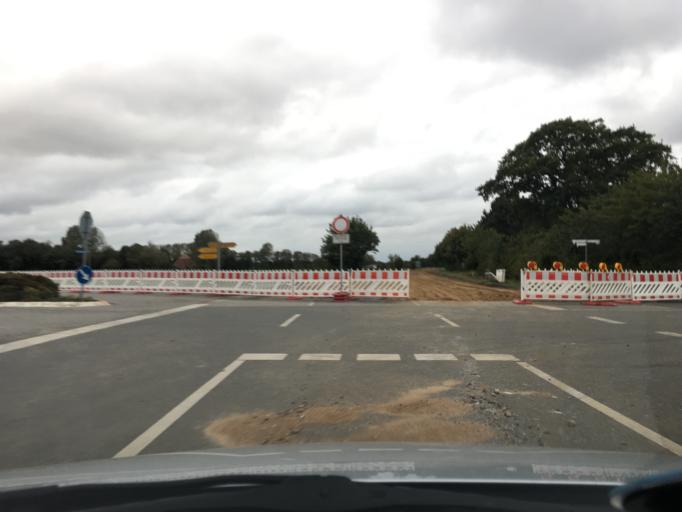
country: DE
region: Schleswig-Holstein
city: Osdorf
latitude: 54.4650
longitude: 10.0449
